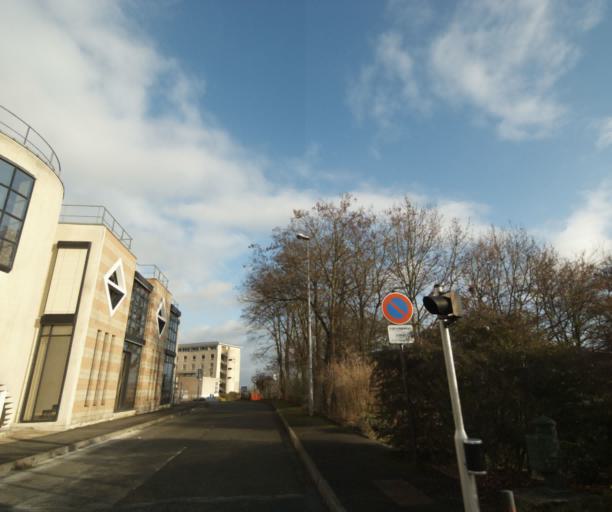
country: FR
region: Pays de la Loire
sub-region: Departement de la Sarthe
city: La Chapelle-Saint-Aubin
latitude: 48.0186
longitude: 0.1616
